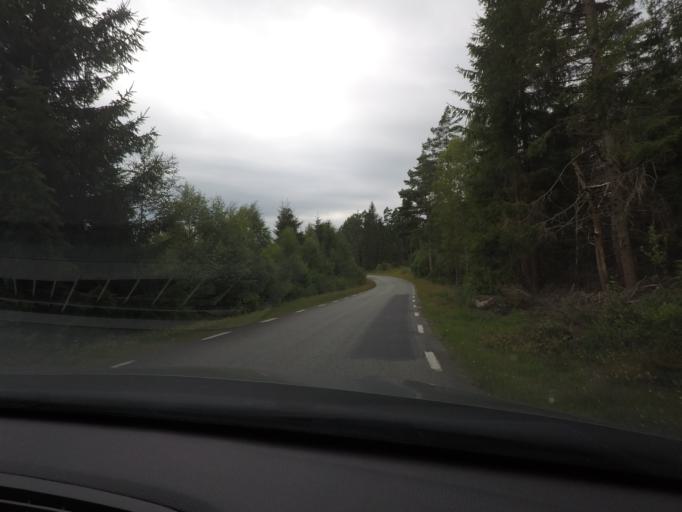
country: SE
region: Kronoberg
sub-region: Markaryds Kommun
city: Stromsnasbruk
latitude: 56.4246
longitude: 13.7815
